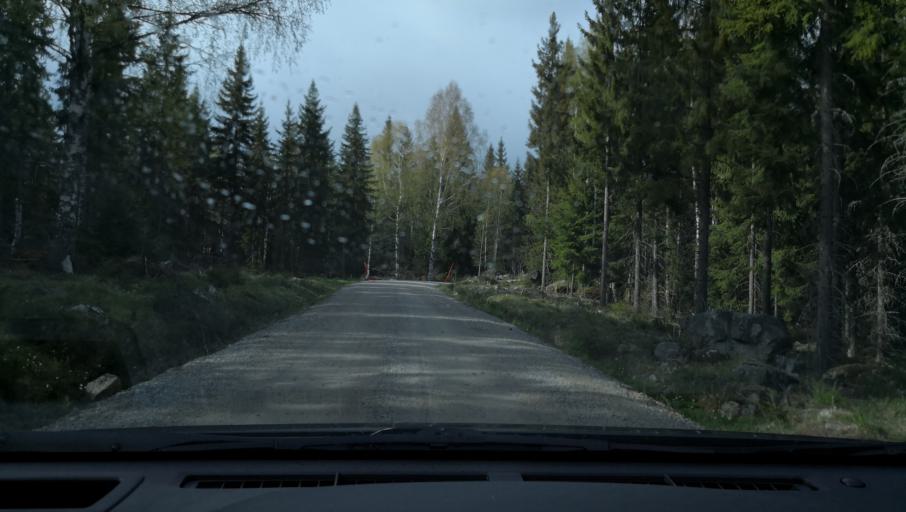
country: SE
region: Vaestmanland
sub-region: Fagersta Kommun
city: Fagersta
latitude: 60.1564
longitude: 15.6974
